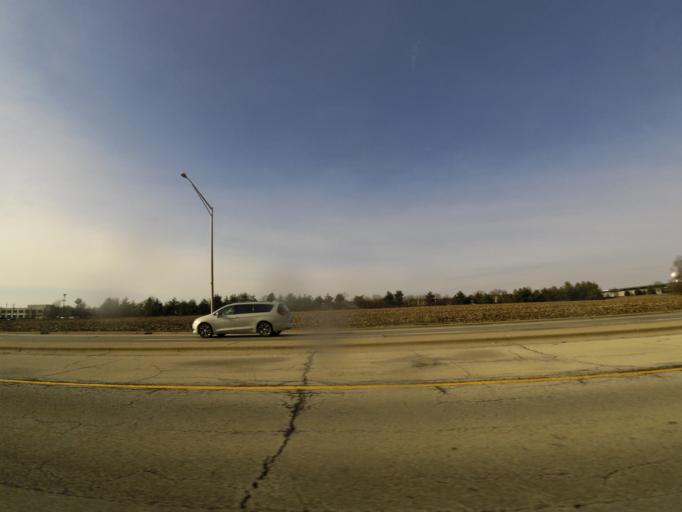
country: US
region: Illinois
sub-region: Macon County
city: Forsyth
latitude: 39.9260
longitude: -88.9555
